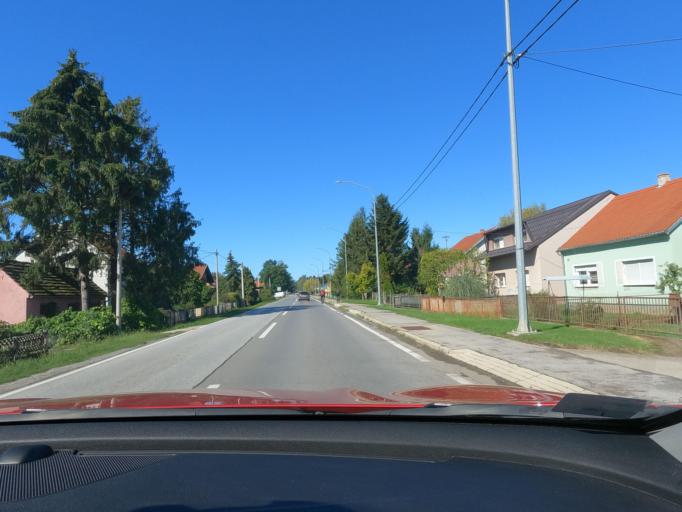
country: HR
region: Sisacko-Moslavacka
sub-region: Grad Sisak
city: Sisak
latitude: 45.4782
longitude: 16.3952
